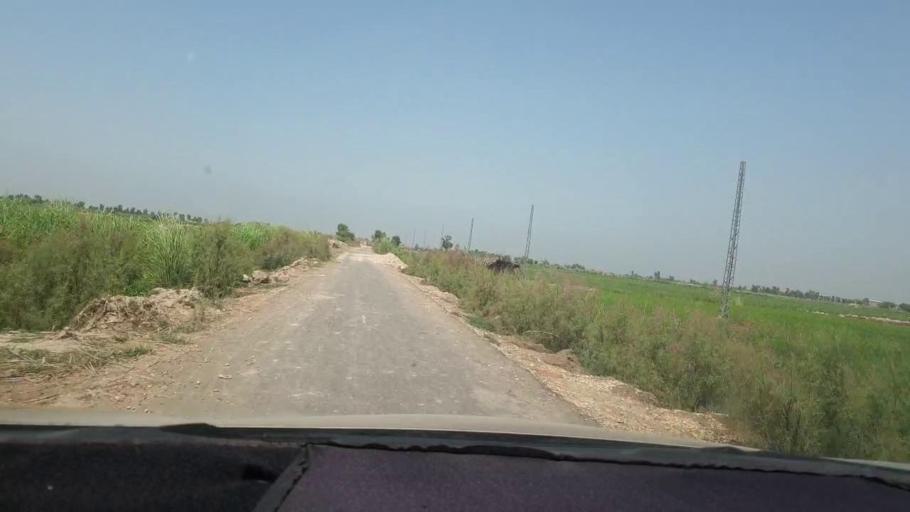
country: PK
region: Sindh
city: Shahdadkot
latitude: 27.8379
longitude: 67.8771
